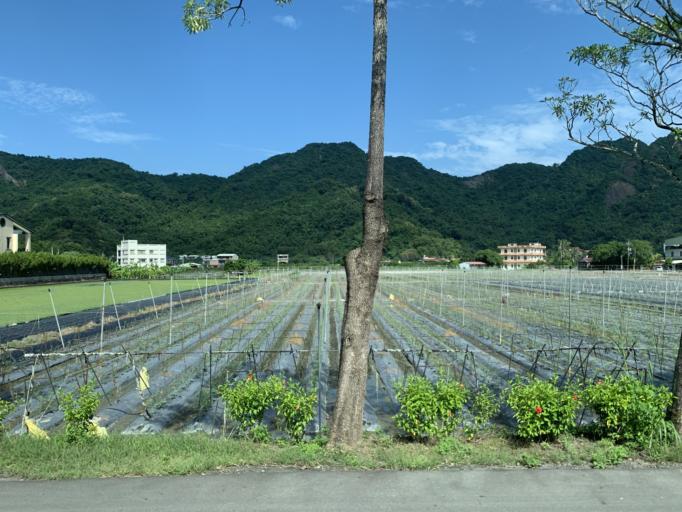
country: TW
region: Taiwan
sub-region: Pingtung
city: Pingtung
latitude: 22.8915
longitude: 120.5095
